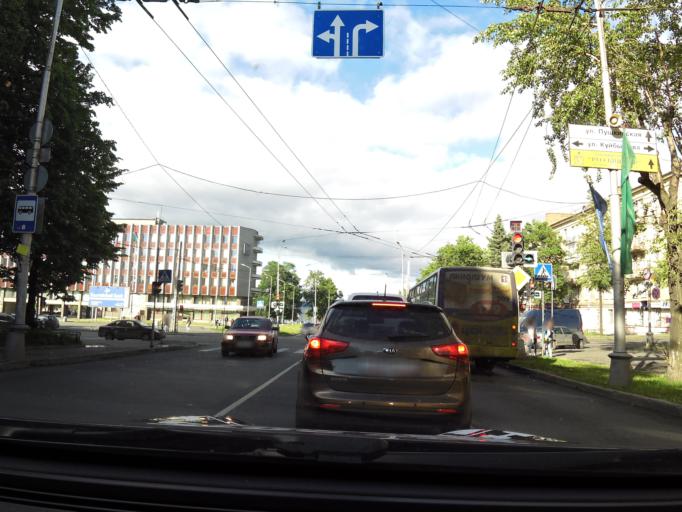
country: RU
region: Republic of Karelia
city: Petrozavodsk
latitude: 61.7930
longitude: 34.3726
